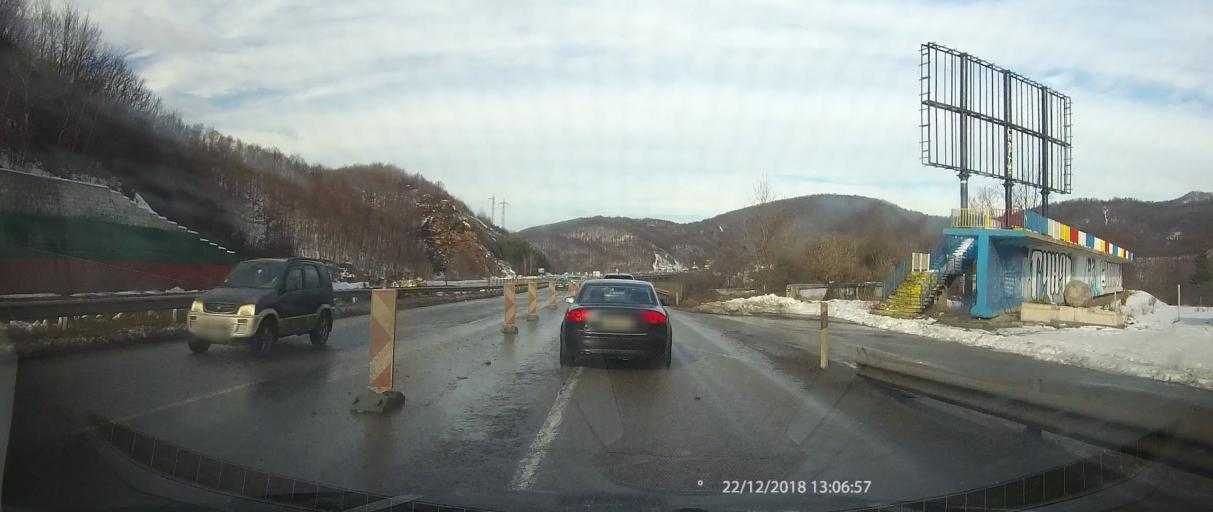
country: BG
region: Sofiya
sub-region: Obshtina Botevgrad
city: Botevgrad
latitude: 42.8176
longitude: 23.7984
